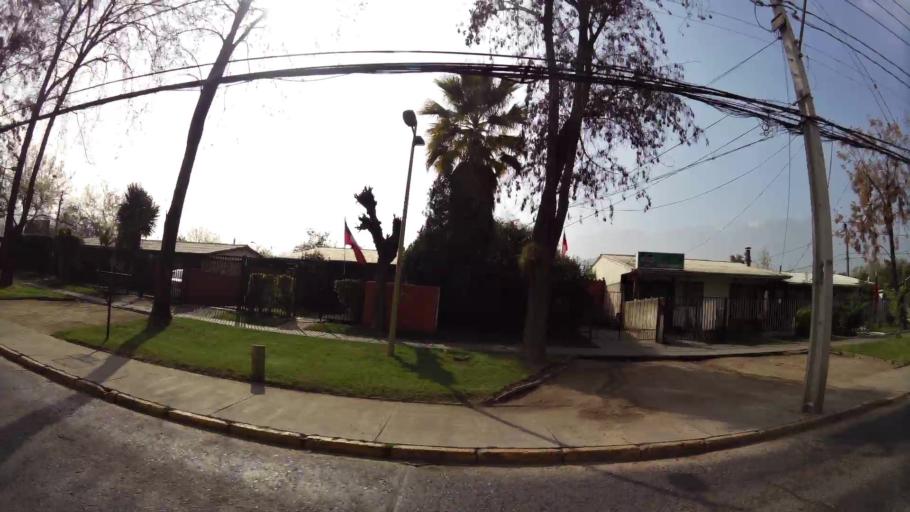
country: CL
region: Santiago Metropolitan
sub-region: Provincia de Santiago
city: Villa Presidente Frei, Nunoa, Santiago, Chile
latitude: -33.4220
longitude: -70.5376
